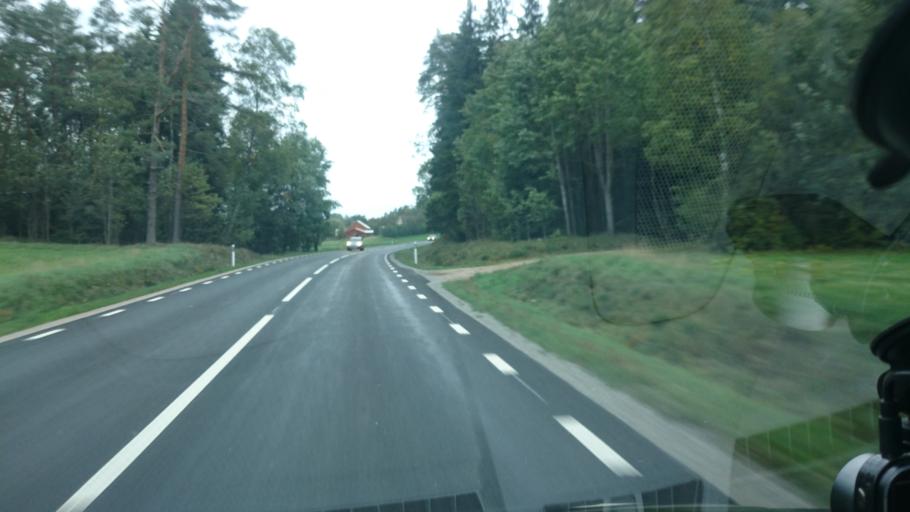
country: SE
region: Vaestra Goetaland
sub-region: Svenljunga Kommun
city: Svenljunga
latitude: 57.5316
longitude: 13.1138
